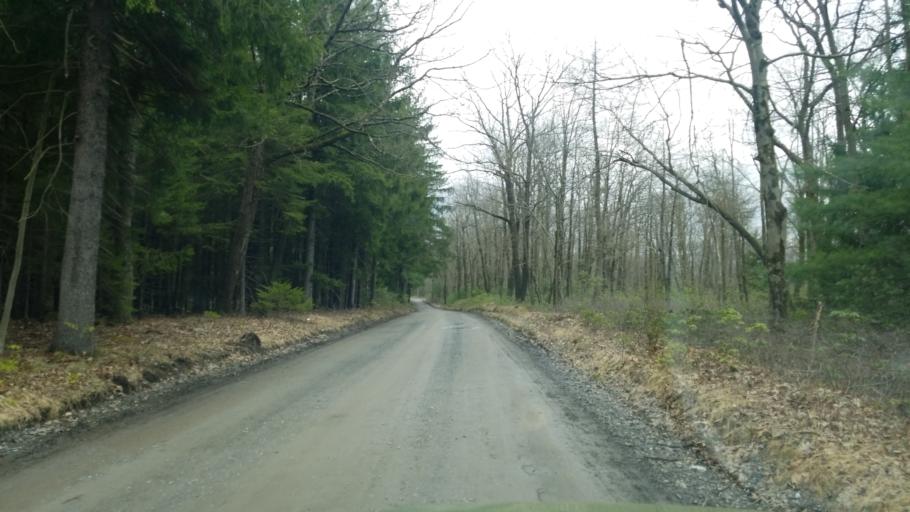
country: US
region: Pennsylvania
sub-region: Clearfield County
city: Shiloh
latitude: 41.1694
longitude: -78.2795
